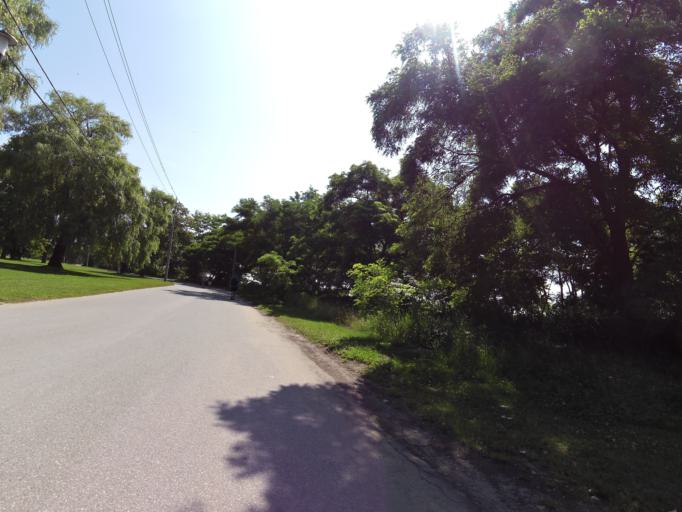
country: CA
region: Ontario
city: Toronto
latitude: 43.6140
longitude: -79.3793
